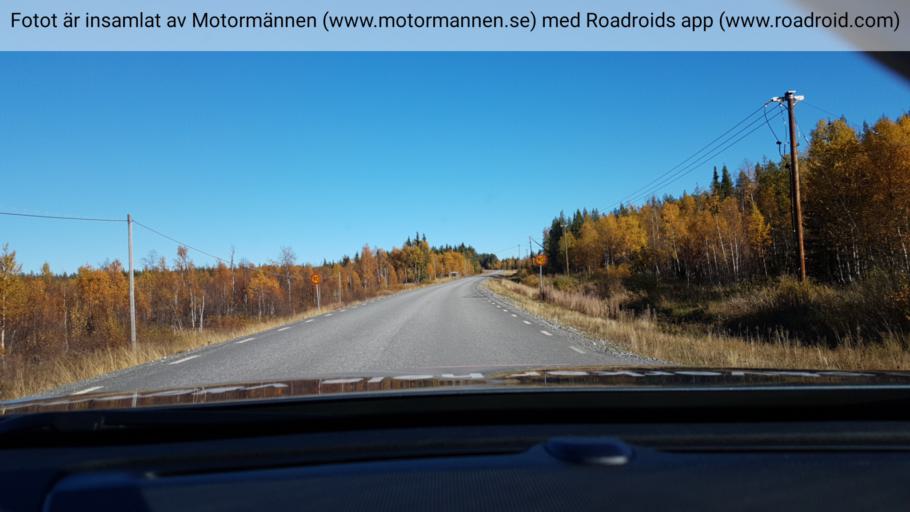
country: SE
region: Norrbotten
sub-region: Gallivare Kommun
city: Gaellivare
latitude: 66.7657
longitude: 21.0346
